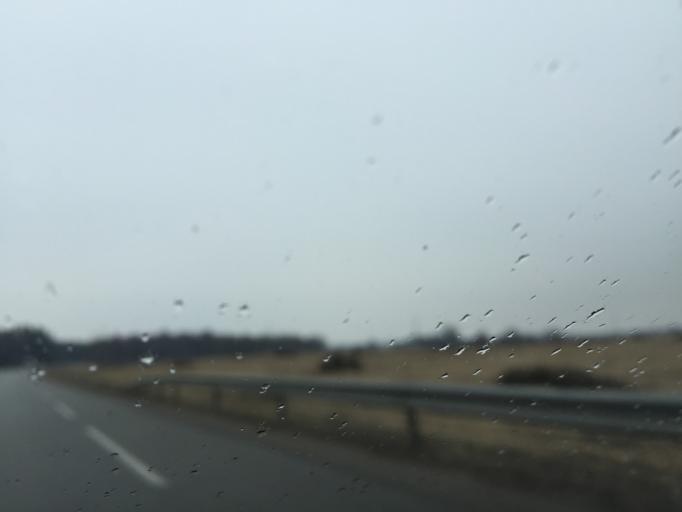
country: LV
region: Saulkrastu
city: Saulkrasti
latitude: 57.4146
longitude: 24.4302
